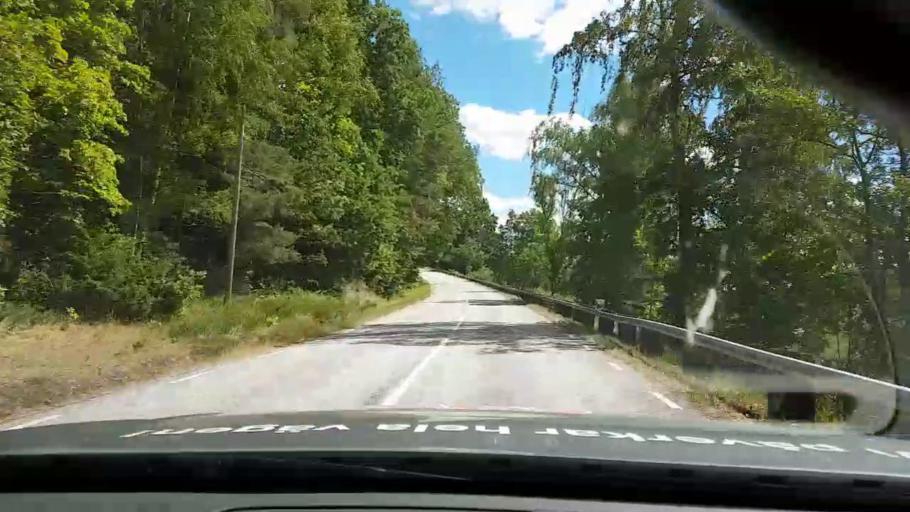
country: SE
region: Kalmar
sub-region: Vasterviks Kommun
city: Overum
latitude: 58.0751
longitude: 16.3634
